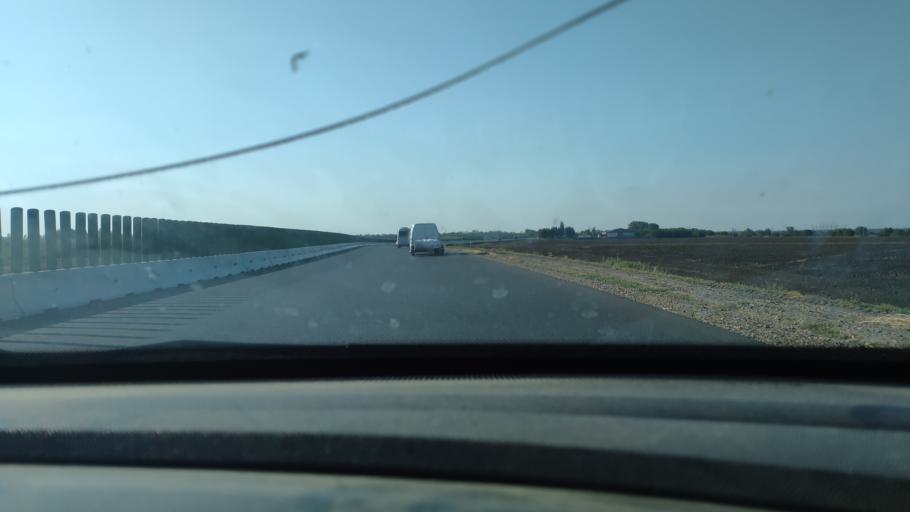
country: RU
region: Krasnodarskiy
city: Medvedovskaya
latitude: 45.4686
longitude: 38.9795
